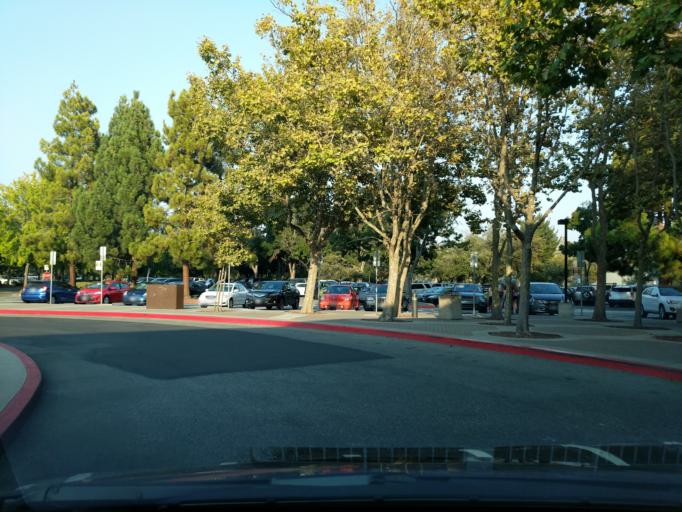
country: US
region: California
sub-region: Santa Clara County
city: Mountain View
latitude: 37.4147
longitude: -122.0806
